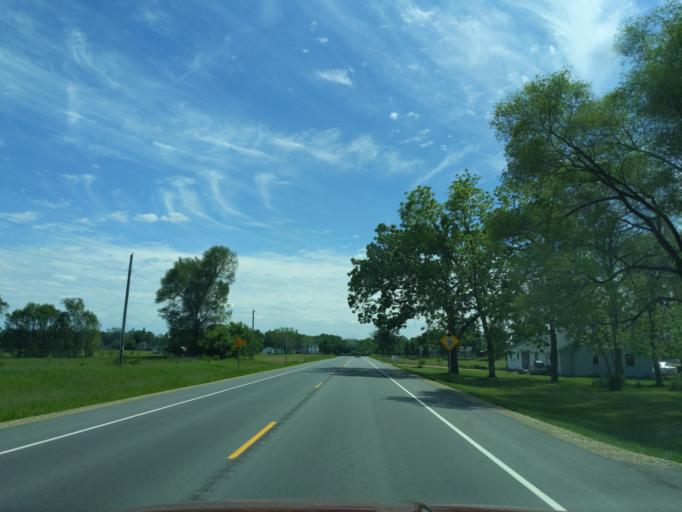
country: US
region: Wisconsin
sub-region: Columbia County
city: Pardeeville
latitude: 43.5514
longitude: -89.3059
